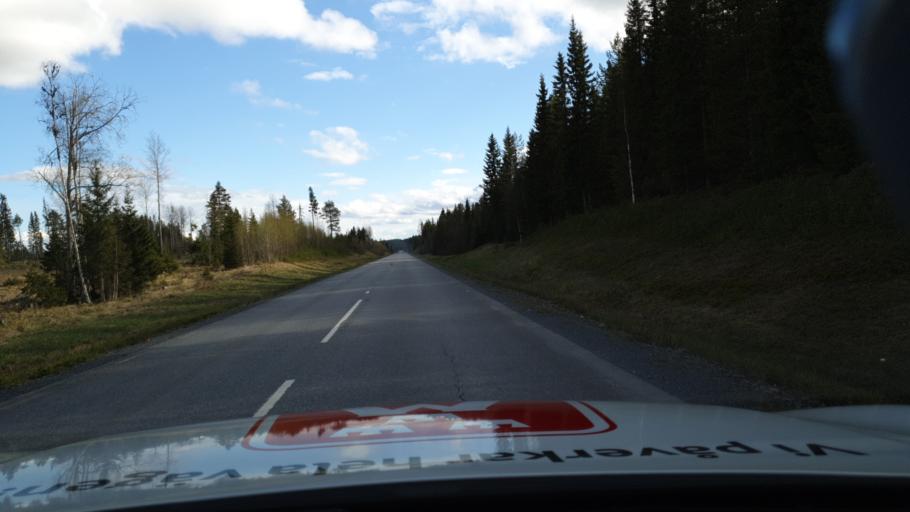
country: SE
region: Jaemtland
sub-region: Krokoms Kommun
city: Krokom
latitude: 63.2865
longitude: 14.4426
